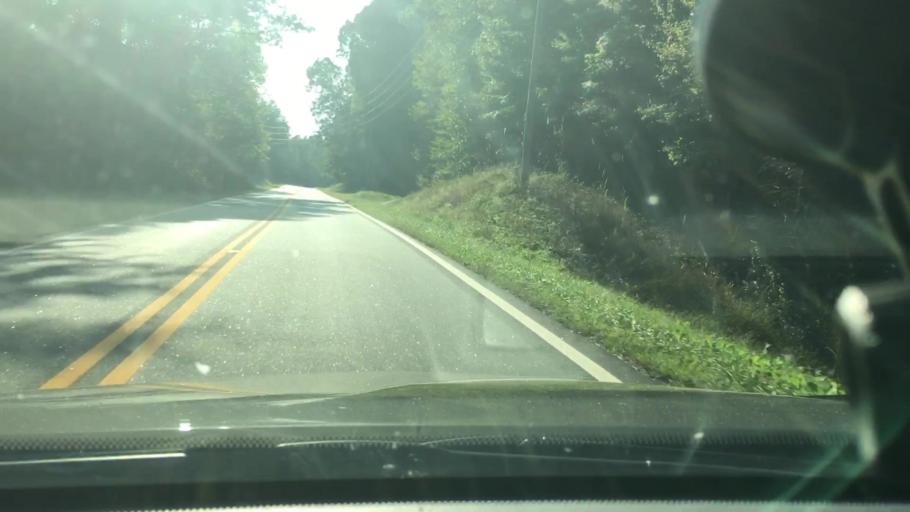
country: US
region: North Carolina
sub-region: Rutherford County
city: Rutherfordton
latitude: 35.3303
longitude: -82.0571
